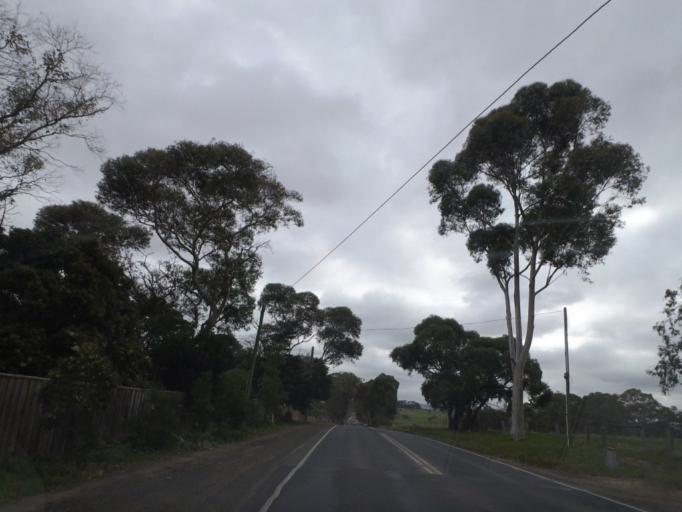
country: AU
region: Victoria
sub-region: Nillumbik
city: Doreen
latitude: -37.6089
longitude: 145.1375
